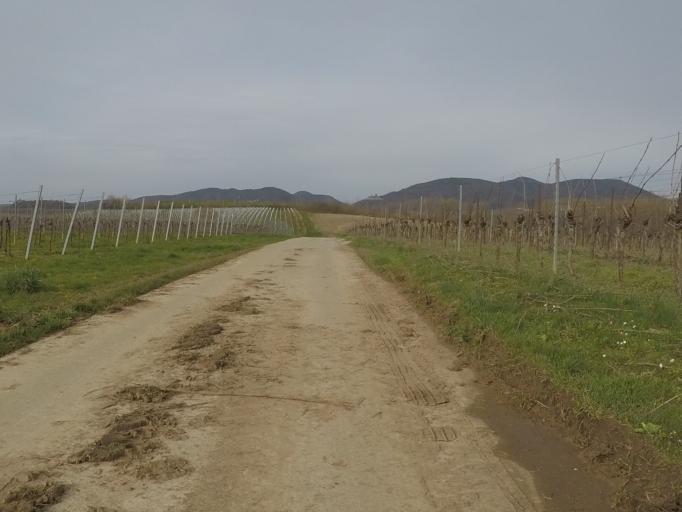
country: DE
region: Rheinland-Pfalz
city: Heuchelheim-Klingen
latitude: 49.1390
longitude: 8.0520
